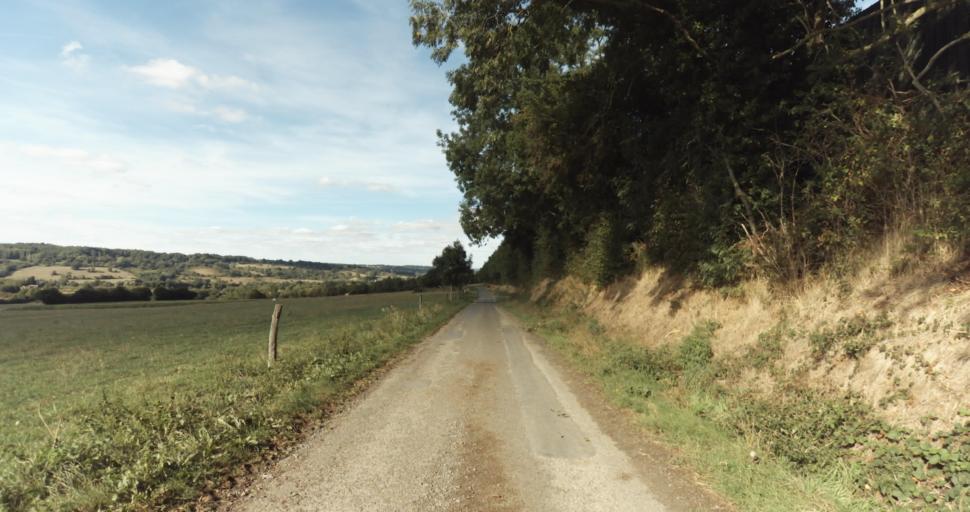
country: FR
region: Lower Normandy
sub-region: Departement de l'Orne
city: Vimoutiers
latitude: 48.9291
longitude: 0.1191
